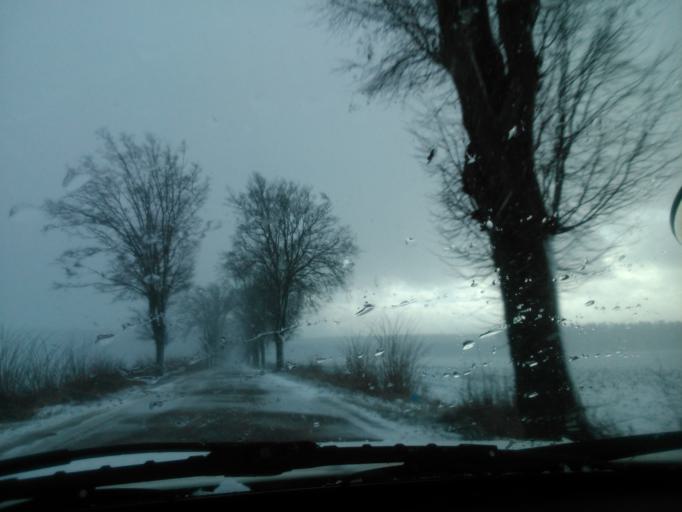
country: PL
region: Kujawsko-Pomorskie
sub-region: Powiat wabrzeski
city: Debowa Laka
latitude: 53.1991
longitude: 19.1626
